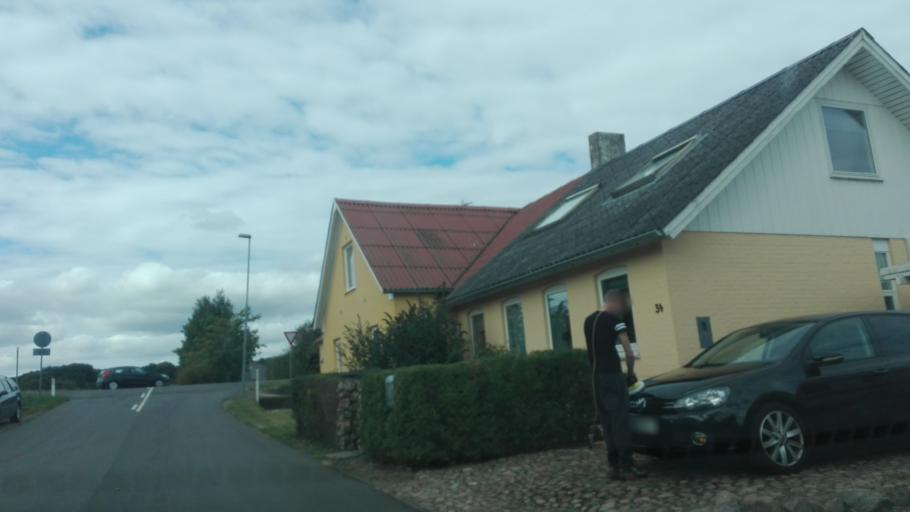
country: DK
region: Central Jutland
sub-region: Skanderborg Kommune
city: Stilling
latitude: 56.0957
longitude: 9.9716
